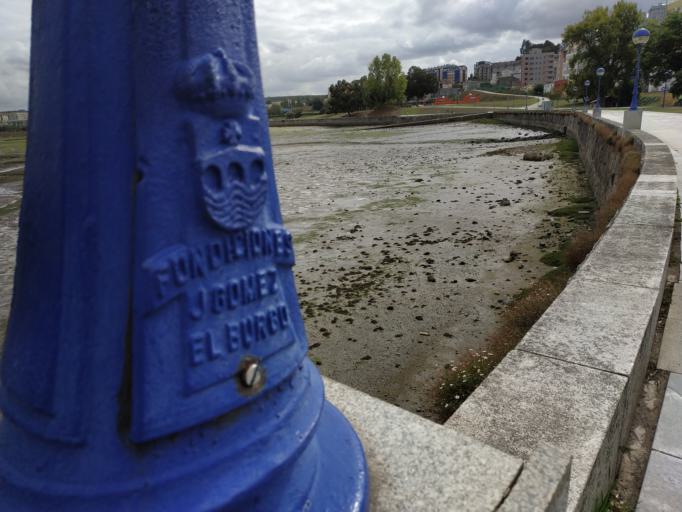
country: ES
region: Galicia
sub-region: Provincia da Coruna
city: Culleredo
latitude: 43.3268
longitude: -8.3801
